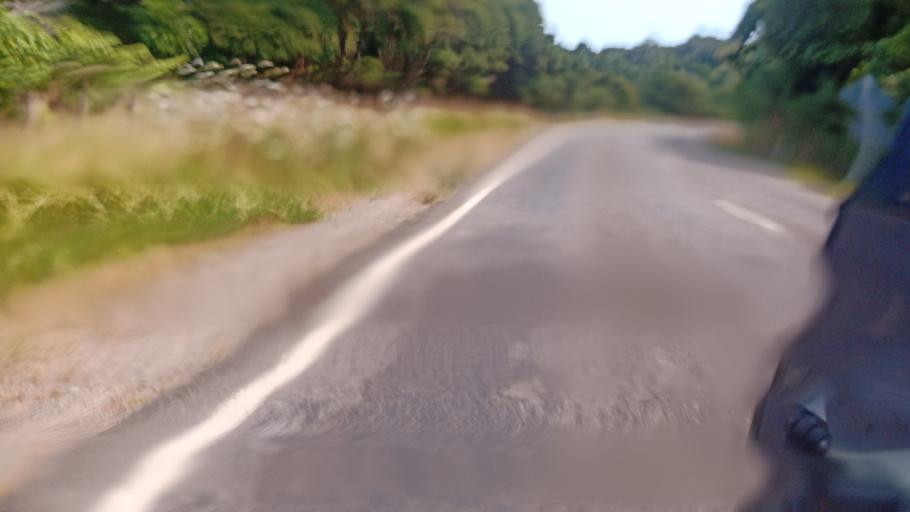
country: NZ
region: Bay of Plenty
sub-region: Opotiki District
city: Opotiki
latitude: -37.5773
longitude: 178.0475
